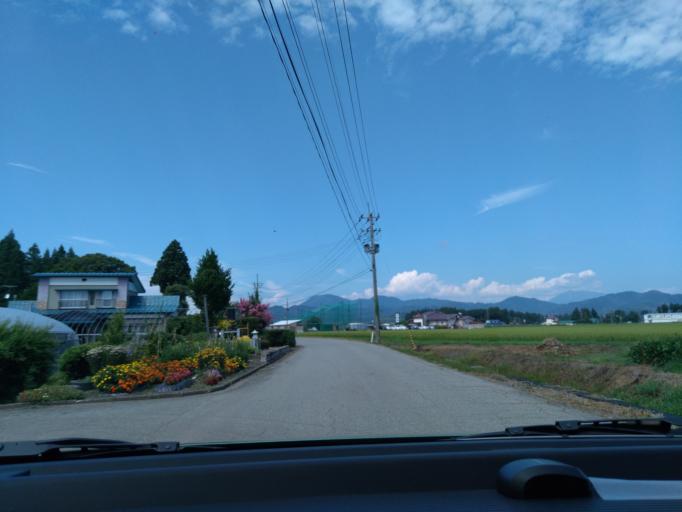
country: JP
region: Akita
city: Kakunodatemachi
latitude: 39.6112
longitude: 140.5944
